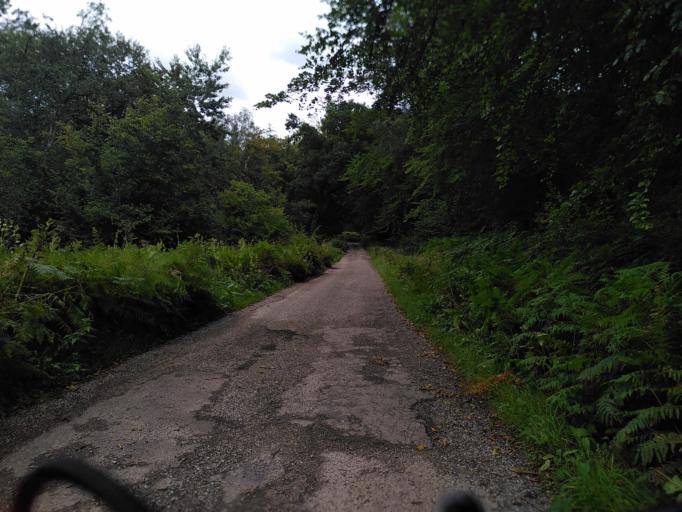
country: FR
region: Nord-Pas-de-Calais
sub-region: Departement du Pas-de-Calais
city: Desvres
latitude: 50.6869
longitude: 1.8247
